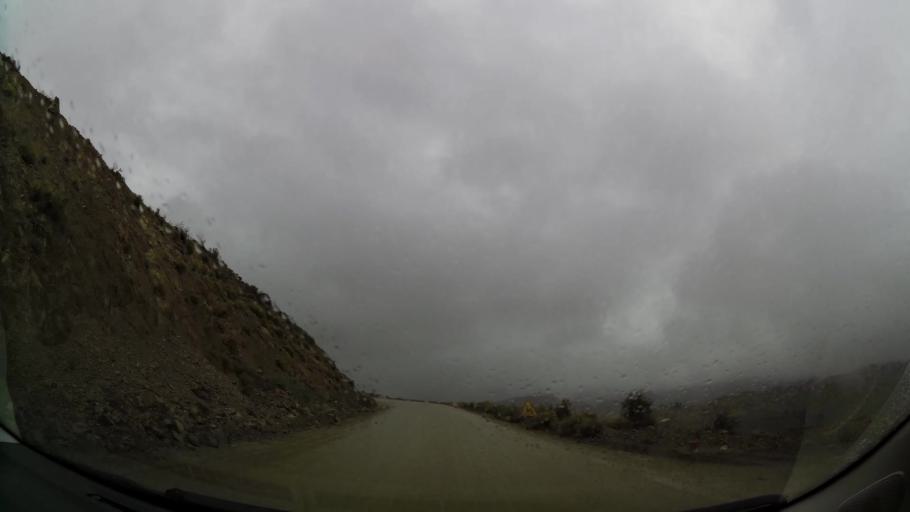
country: MA
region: Oriental
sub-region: Nador
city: Midar
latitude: 34.8970
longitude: -3.7778
